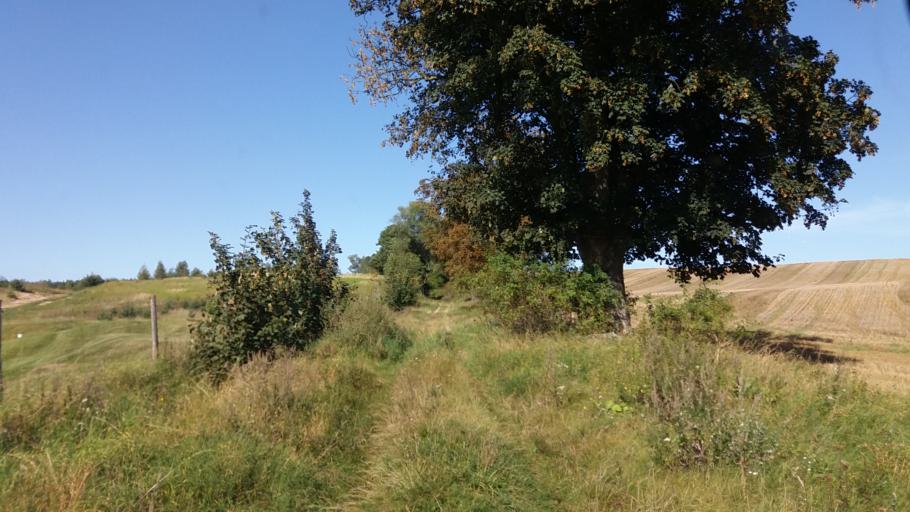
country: PL
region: West Pomeranian Voivodeship
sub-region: Powiat choszczenski
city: Krzecin
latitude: 53.1290
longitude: 15.5019
